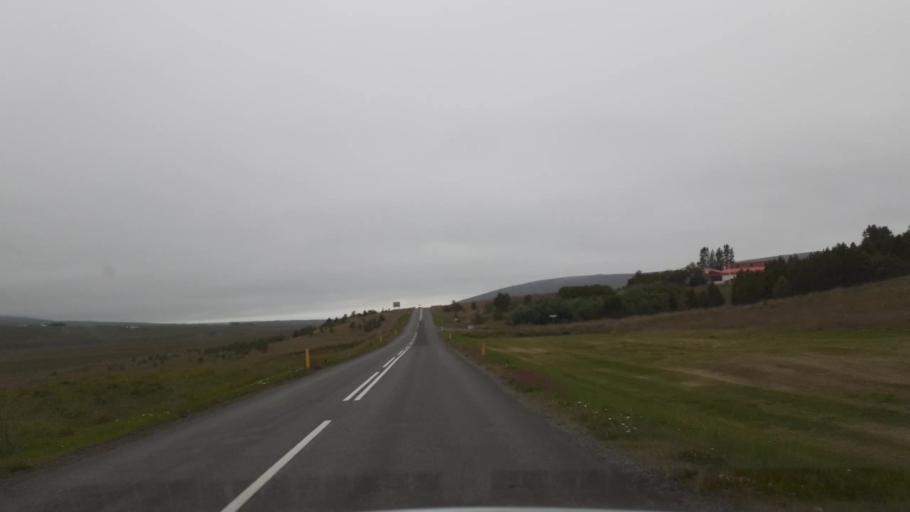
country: IS
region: Northeast
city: Siglufjoerdur
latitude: 65.7350
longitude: -19.1213
